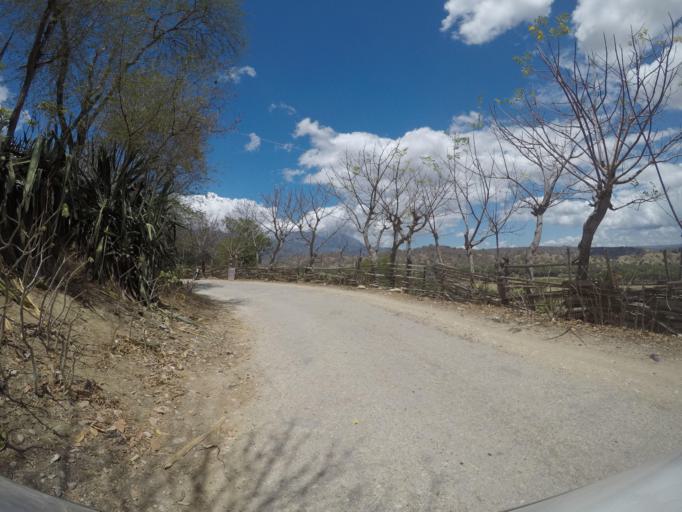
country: TL
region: Baucau
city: Baucau
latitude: -8.4783
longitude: 126.6024
